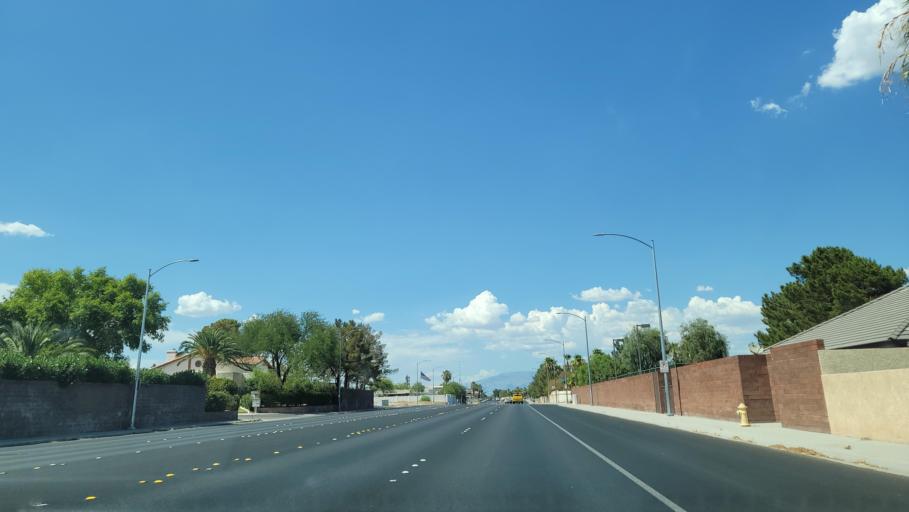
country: US
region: Nevada
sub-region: Clark County
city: Spring Valley
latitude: 36.1388
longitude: -115.2609
